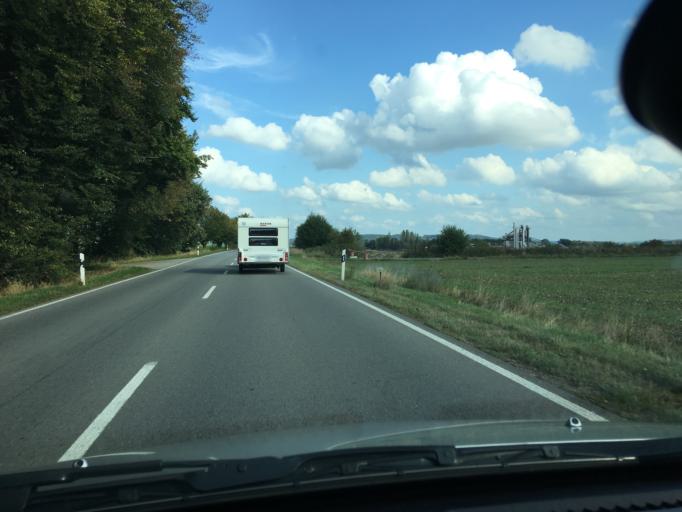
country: DE
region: Baden-Wuerttemberg
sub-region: Tuebingen Region
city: Ingoldingen
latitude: 48.0244
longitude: 9.7171
